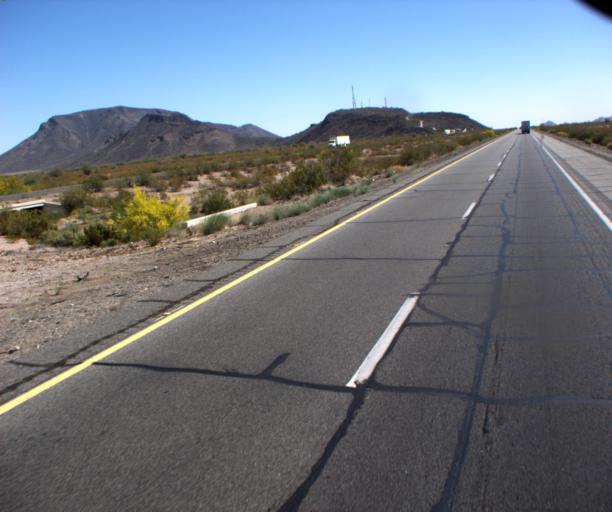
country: US
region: Arizona
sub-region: La Paz County
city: Salome
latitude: 33.5318
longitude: -113.1307
